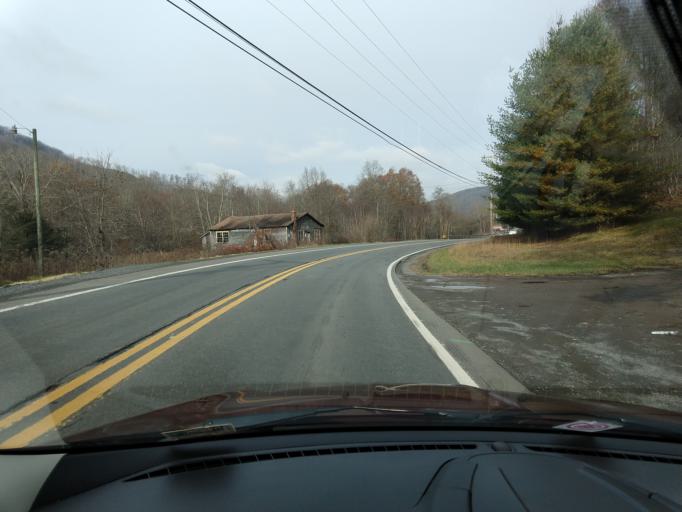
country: US
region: West Virginia
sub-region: Greenbrier County
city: Rainelle
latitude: 37.9718
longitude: -80.7075
